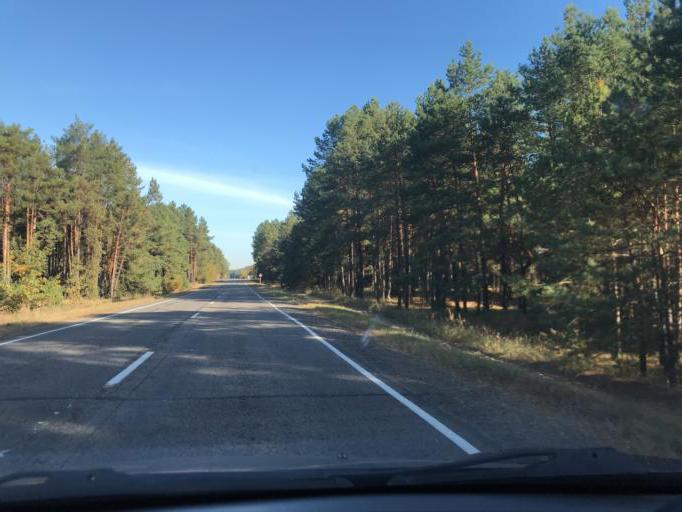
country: UA
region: Chernihiv
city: Lyubech
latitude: 51.6175
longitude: 30.4777
